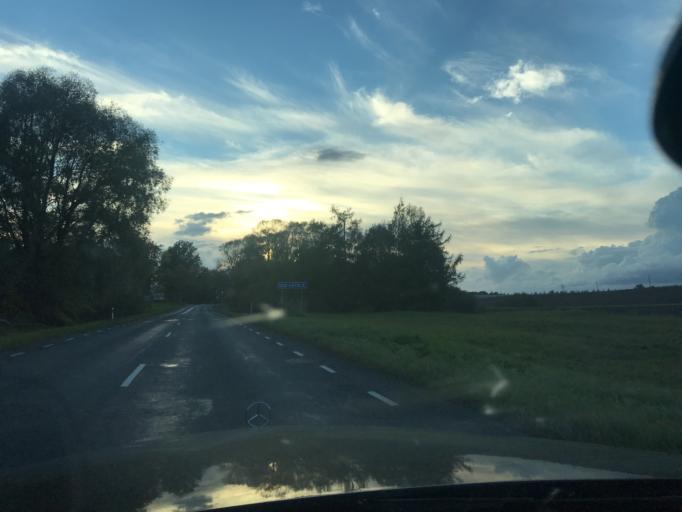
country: EE
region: Vorumaa
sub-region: Antsla vald
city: Vana-Antsla
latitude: 57.8820
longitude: 26.5514
